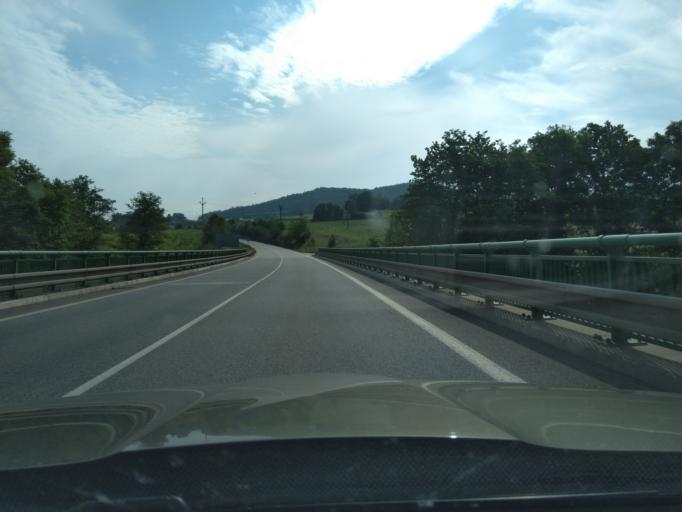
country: CZ
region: Jihocesky
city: Husinec
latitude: 49.0485
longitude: 14.0236
